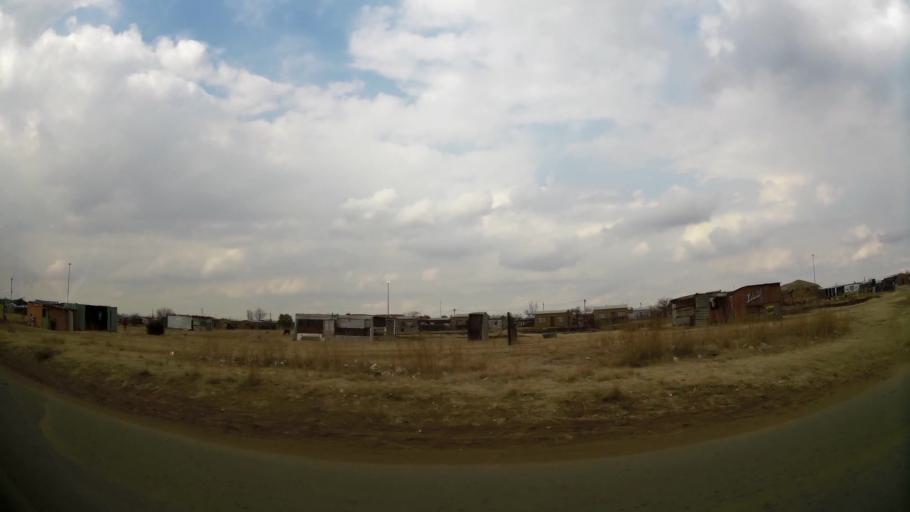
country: ZA
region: Orange Free State
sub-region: Fezile Dabi District Municipality
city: Sasolburg
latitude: -26.8558
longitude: 27.8763
